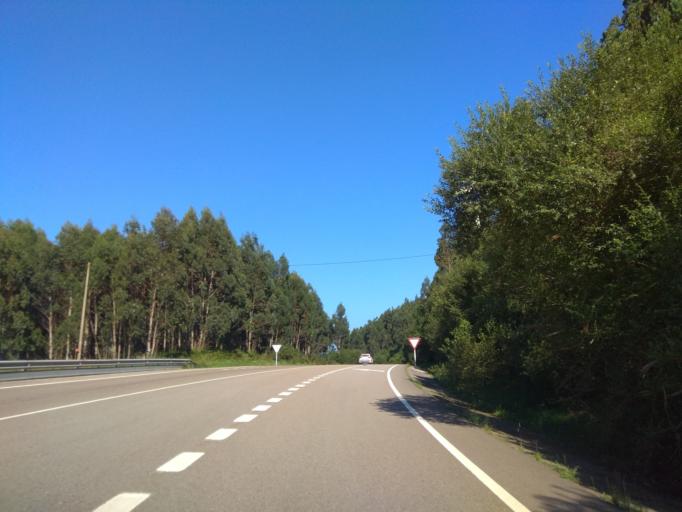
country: ES
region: Cantabria
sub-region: Provincia de Cantabria
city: Bareyo
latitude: 43.4725
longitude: -3.6320
